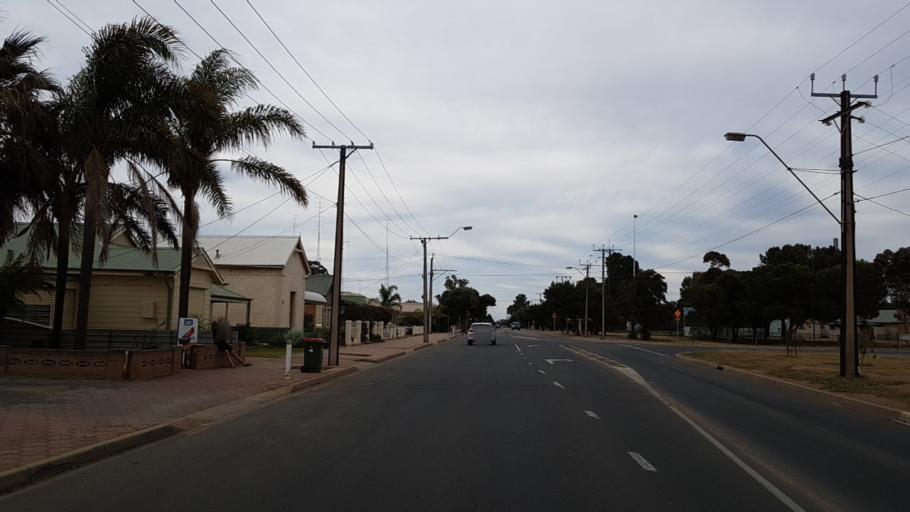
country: AU
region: South Australia
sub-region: Port Pirie City and Dists
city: Port Pirie
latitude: -33.1843
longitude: 138.0039
